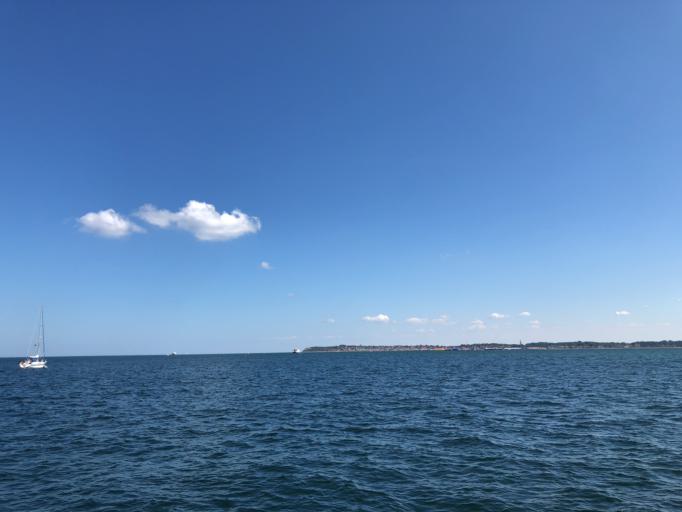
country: DK
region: Capital Region
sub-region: Halsnaes Kommune
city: Hundested
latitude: 55.9478
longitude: 11.8022
